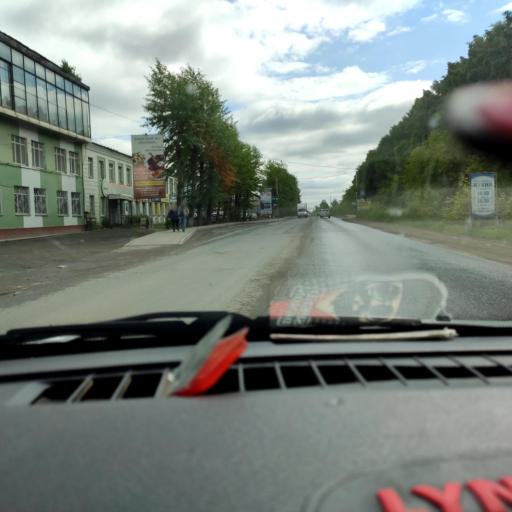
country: RU
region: Perm
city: Perm
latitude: 57.9573
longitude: 56.2152
